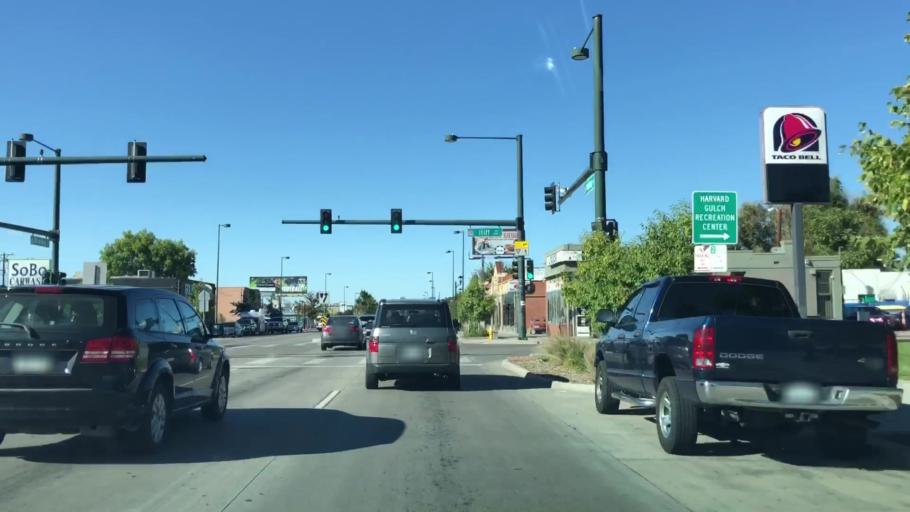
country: US
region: Colorado
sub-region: Arapahoe County
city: Englewood
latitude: 39.6745
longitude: -104.9875
